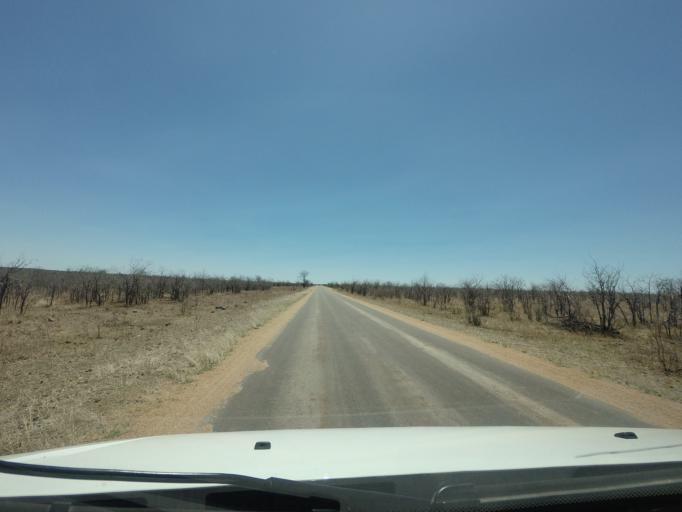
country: ZA
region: Limpopo
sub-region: Mopani District Municipality
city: Phalaborwa
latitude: -23.5756
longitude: 31.4511
